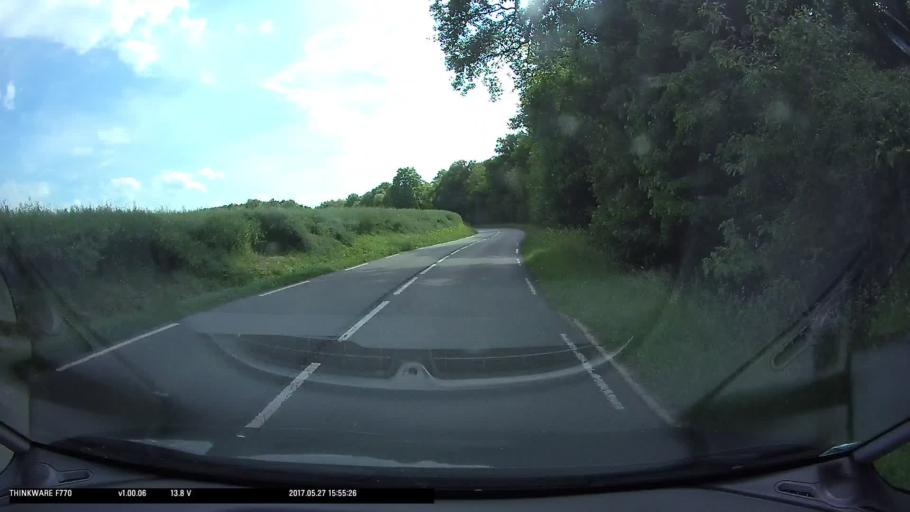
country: FR
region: Ile-de-France
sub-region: Departement du Val-d'Oise
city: Marines
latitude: 49.1263
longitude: 1.9829
